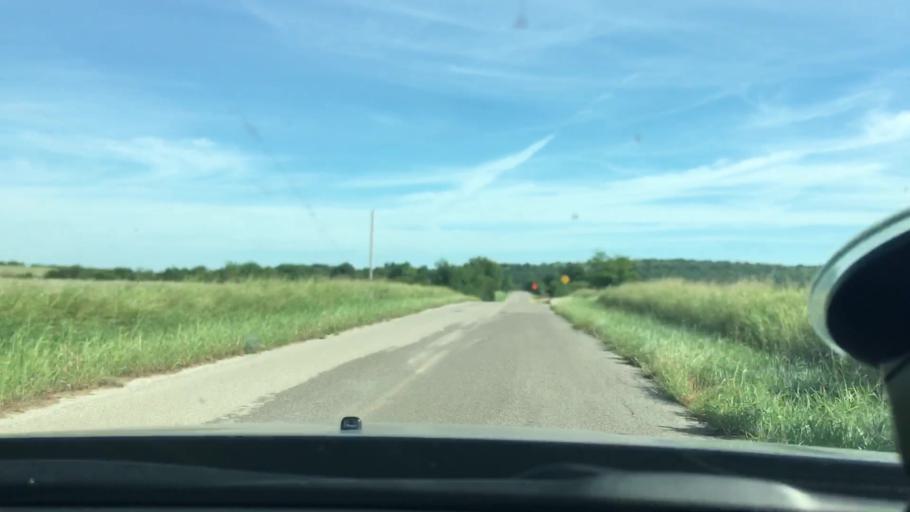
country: US
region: Oklahoma
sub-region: Carter County
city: Lone Grove
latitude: 34.3280
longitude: -97.2825
